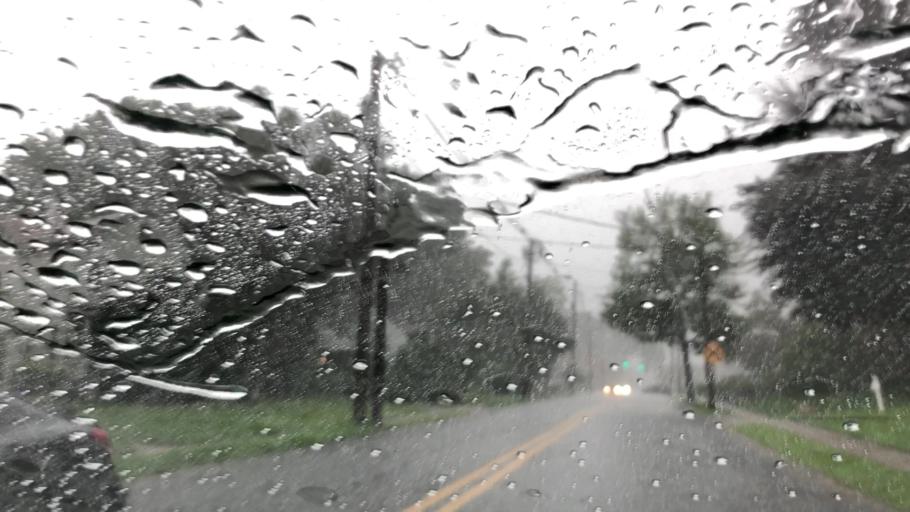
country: US
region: New Jersey
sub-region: Bergen County
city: Rochelle Park
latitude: 40.8983
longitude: -74.0786
